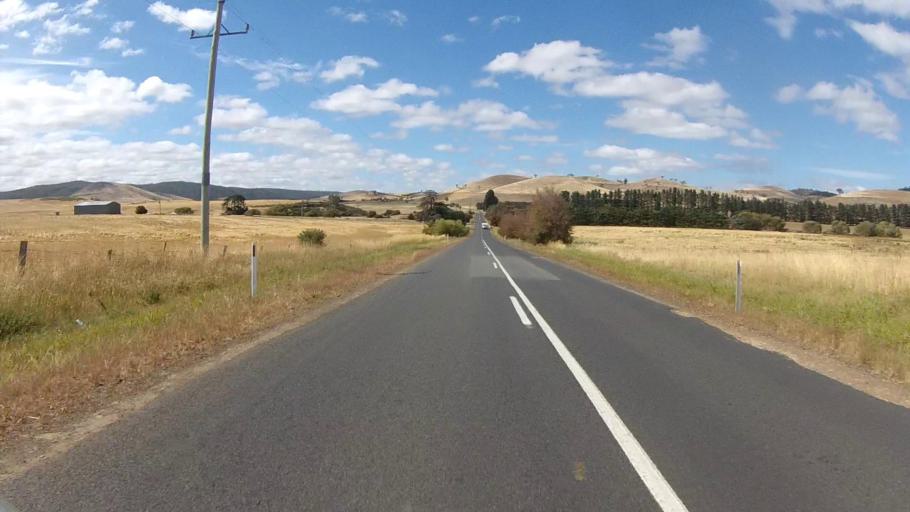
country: AU
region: Tasmania
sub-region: Brighton
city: Bridgewater
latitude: -42.5440
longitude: 147.3729
